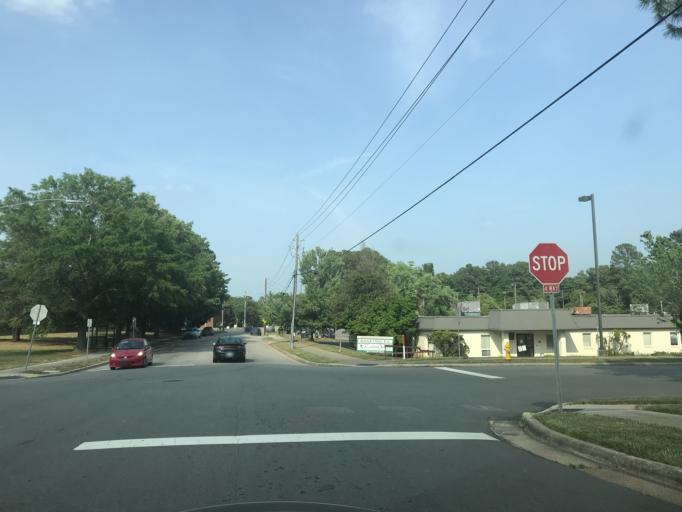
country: US
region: North Carolina
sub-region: Wake County
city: Raleigh
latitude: 35.7816
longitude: -78.5859
